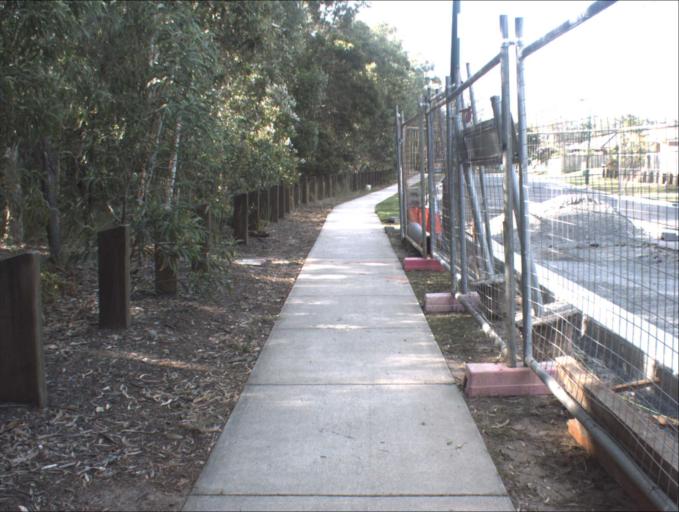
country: AU
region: Queensland
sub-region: Logan
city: Park Ridge South
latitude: -27.6851
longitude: 153.0518
